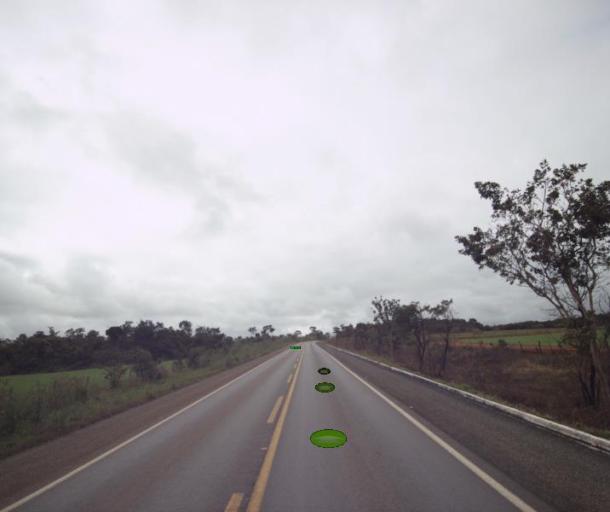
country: BR
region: Goias
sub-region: Uruacu
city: Uruacu
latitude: -14.6731
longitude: -49.1398
